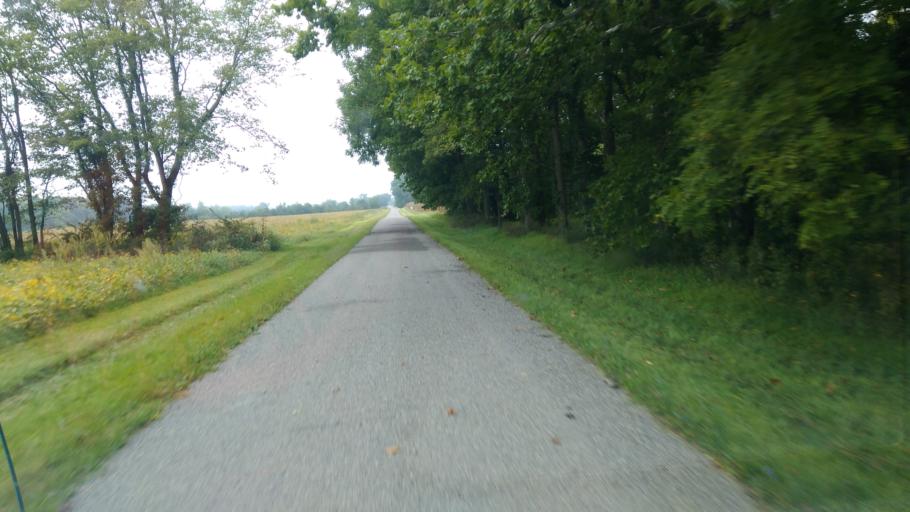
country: US
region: Ohio
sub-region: Logan County
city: Northwood
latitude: 40.4777
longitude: -83.6183
